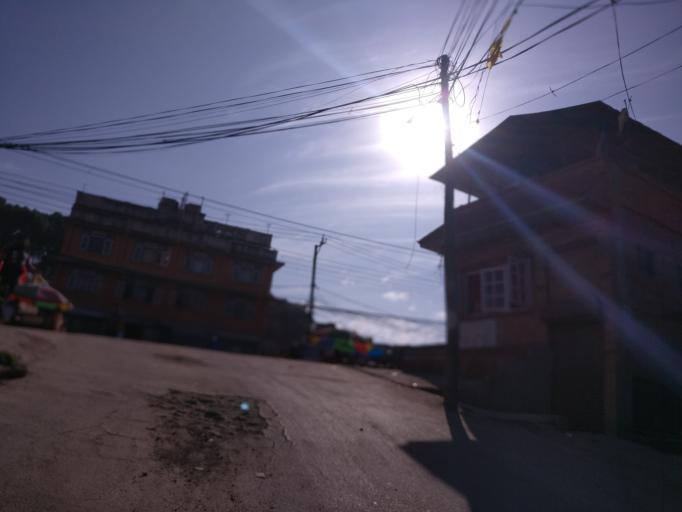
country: NP
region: Central Region
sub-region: Bagmati Zone
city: Patan
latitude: 27.6731
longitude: 85.3339
